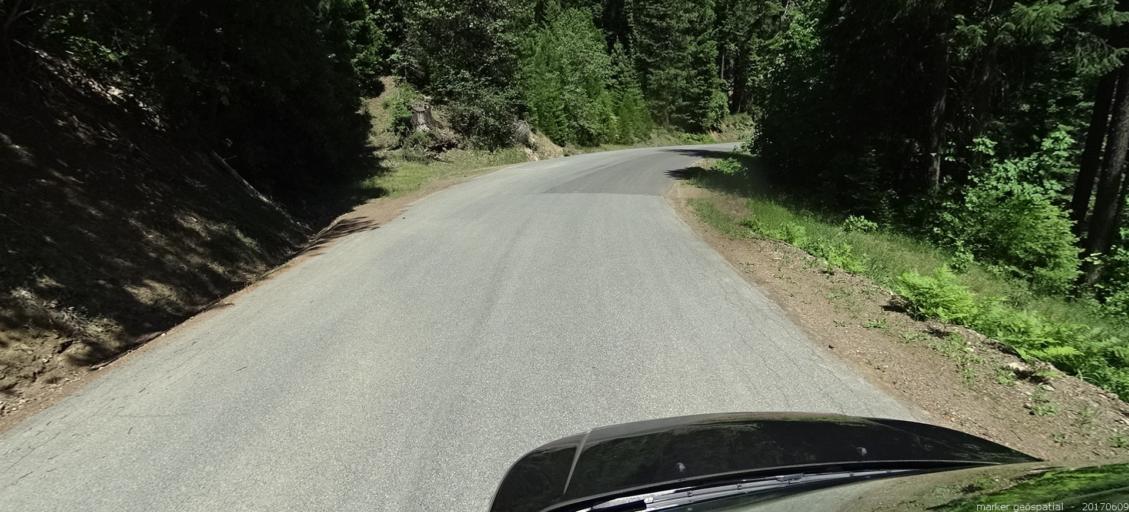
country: US
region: California
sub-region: Siskiyou County
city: Yreka
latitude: 41.4300
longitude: -122.9467
